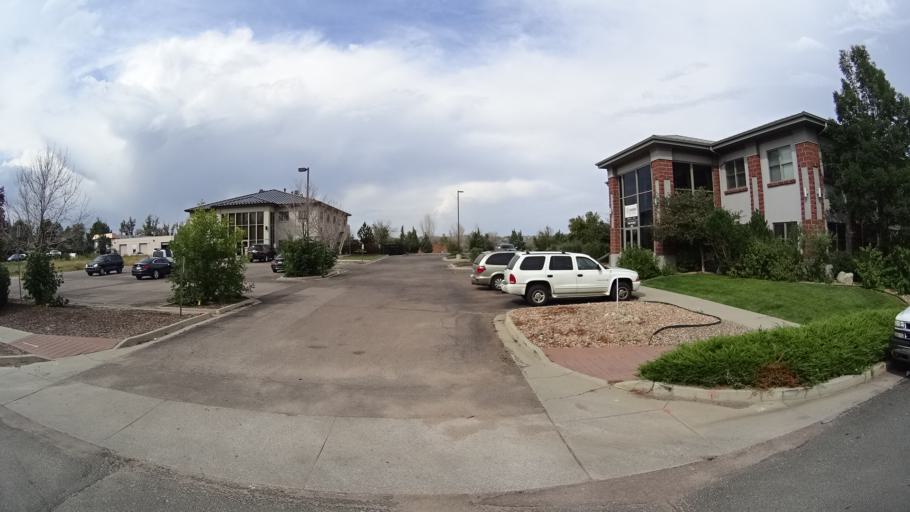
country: US
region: Colorado
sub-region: El Paso County
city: Cimarron Hills
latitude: 38.8796
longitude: -104.7595
